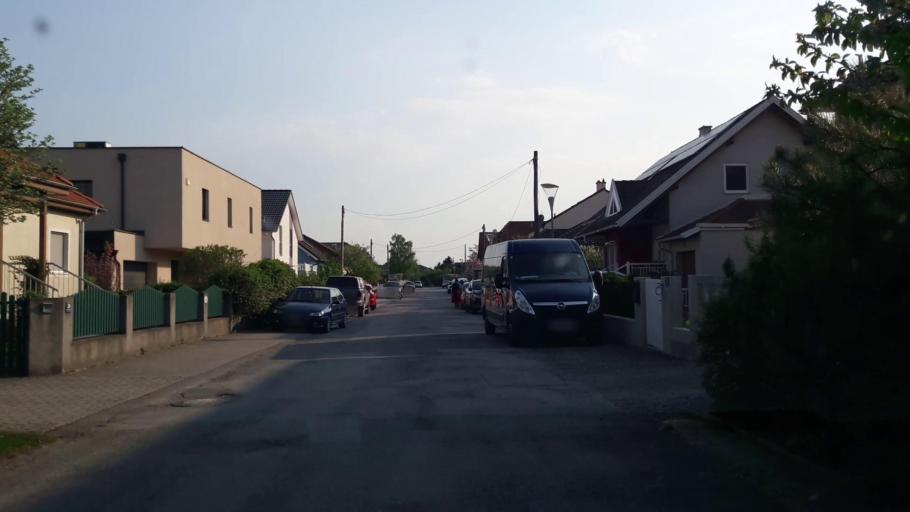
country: AT
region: Lower Austria
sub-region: Politischer Bezirk Ganserndorf
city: Deutsch-Wagram
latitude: 48.3188
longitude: 16.5868
